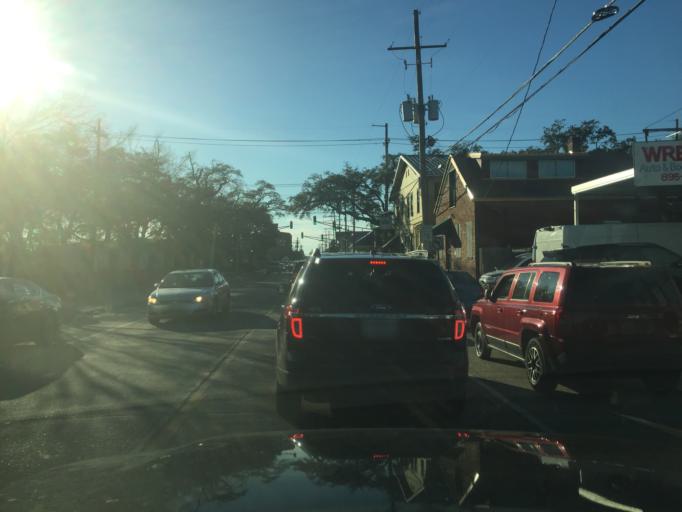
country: US
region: Louisiana
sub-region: Jefferson Parish
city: Marrero
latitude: 29.9172
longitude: -90.1003
